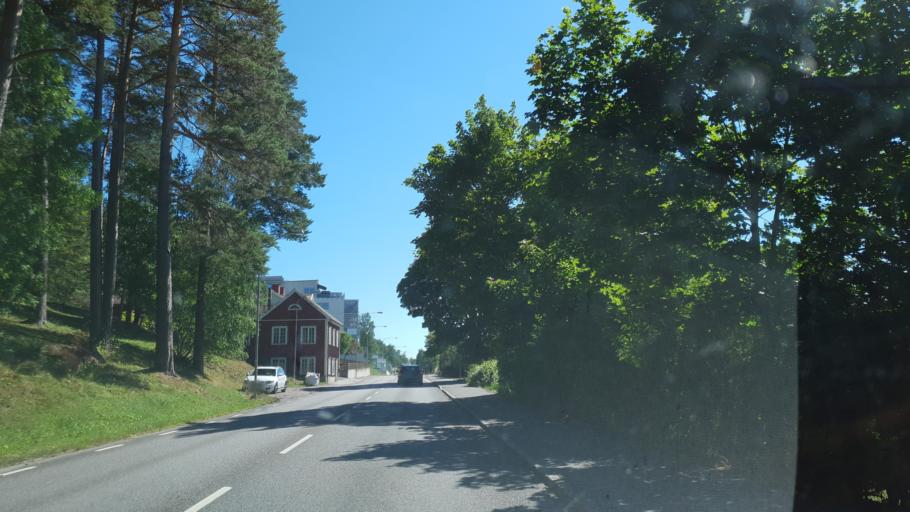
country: SE
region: Joenkoeping
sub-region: Jonkopings Kommun
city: Graenna
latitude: 58.0134
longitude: 14.4585
